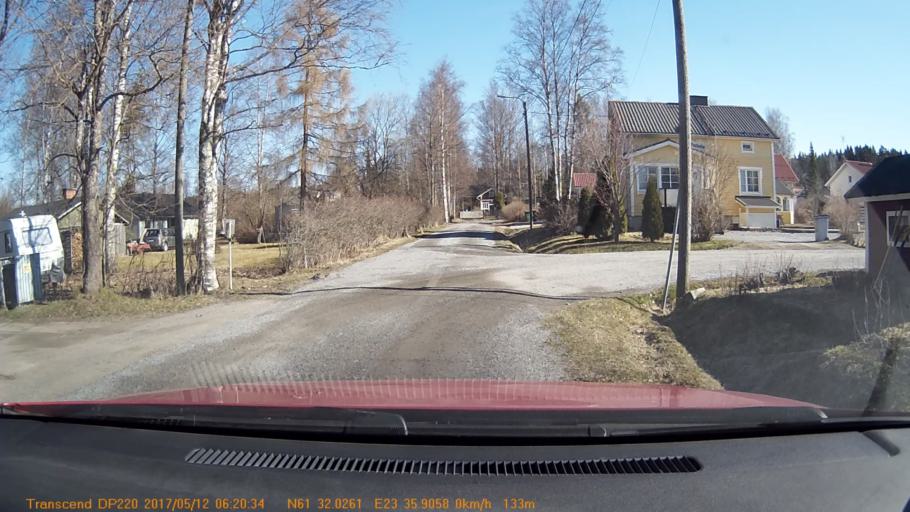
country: FI
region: Pirkanmaa
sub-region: Tampere
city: Yloejaervi
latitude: 61.5338
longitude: 23.5984
